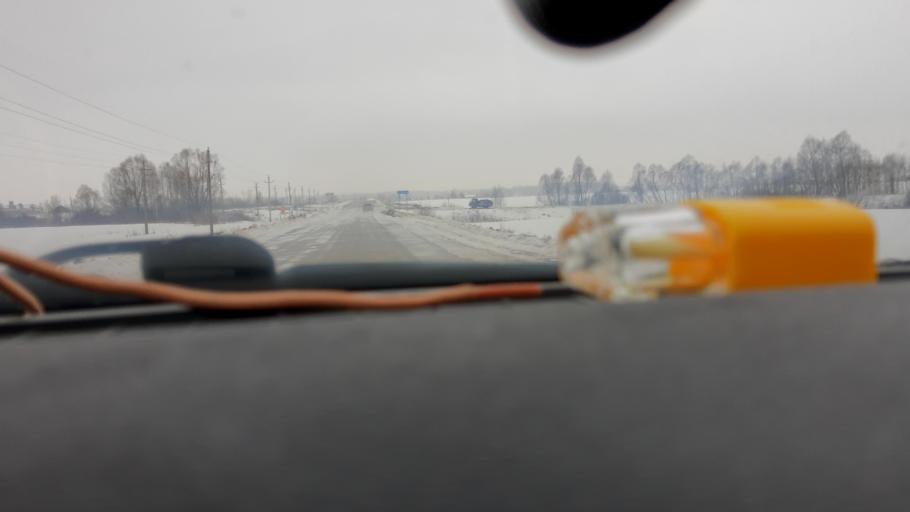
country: RU
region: Bashkortostan
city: Ulukulevo
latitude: 54.5184
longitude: 56.4191
